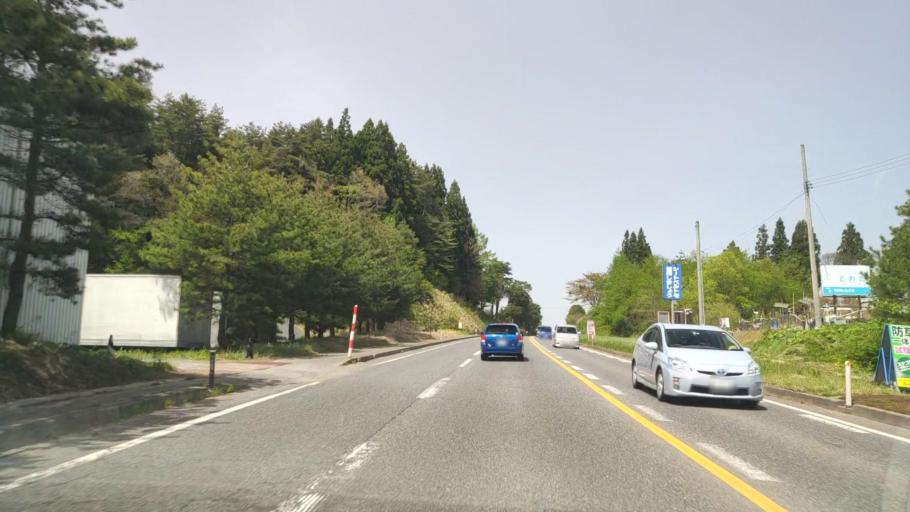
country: JP
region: Aomori
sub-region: Misawa Shi
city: Inuotose
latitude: 40.6659
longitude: 141.1862
